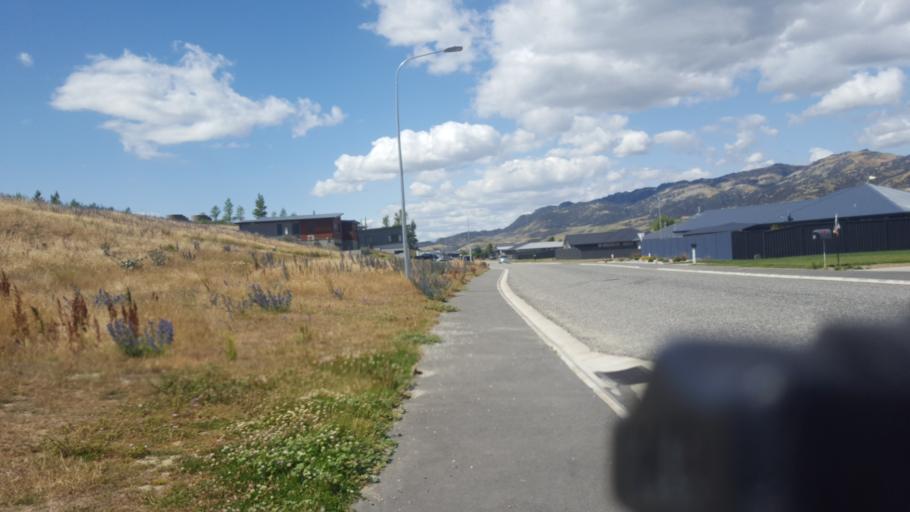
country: NZ
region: Otago
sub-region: Queenstown-Lakes District
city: Wanaka
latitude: -44.9746
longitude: 169.2406
